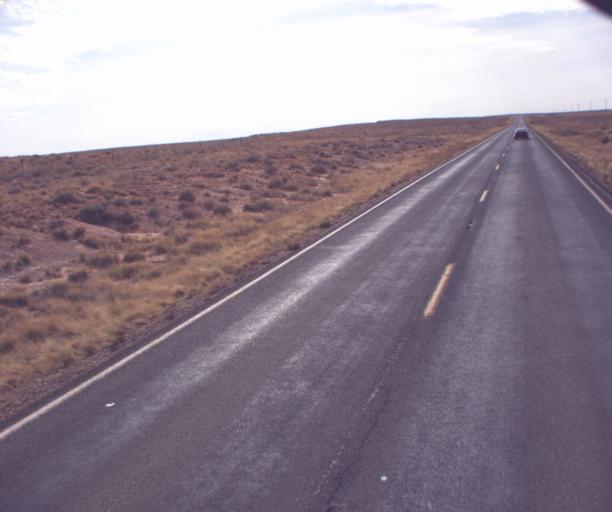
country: US
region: Arizona
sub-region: Apache County
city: Chinle
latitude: 35.9813
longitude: -109.6001
